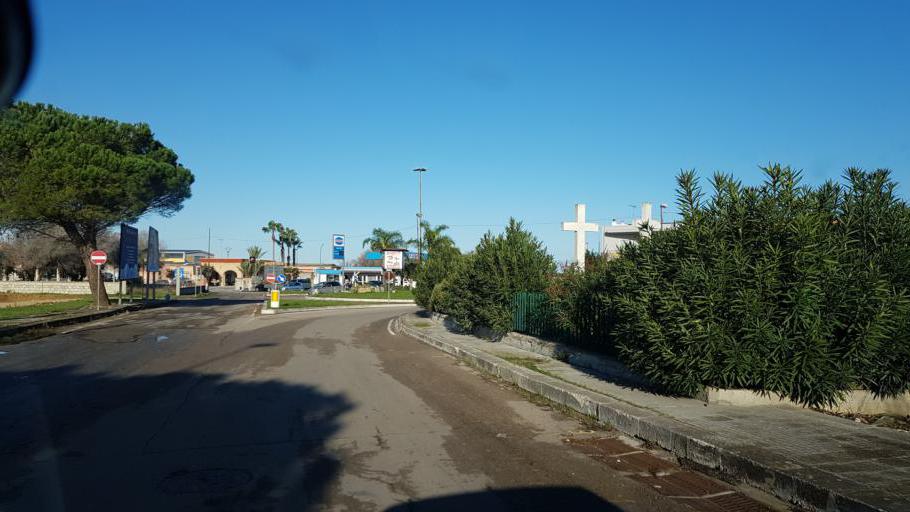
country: IT
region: Apulia
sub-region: Provincia di Brindisi
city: Torchiarolo
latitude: 40.4860
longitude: 18.0460
